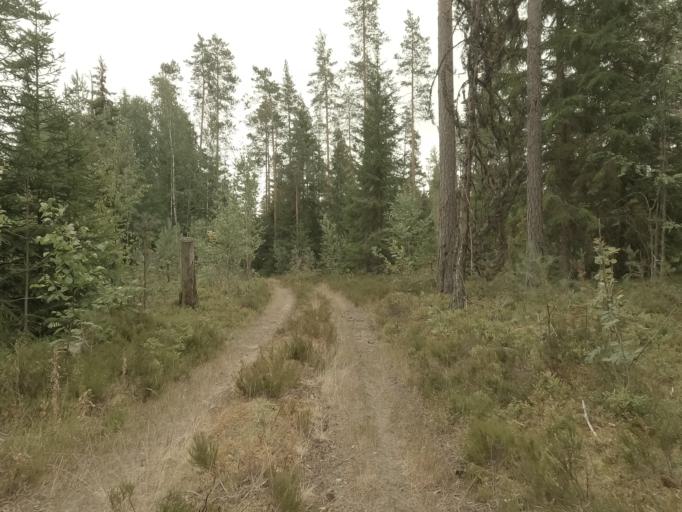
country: RU
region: Leningrad
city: Kamennogorsk
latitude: 61.0517
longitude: 29.1790
